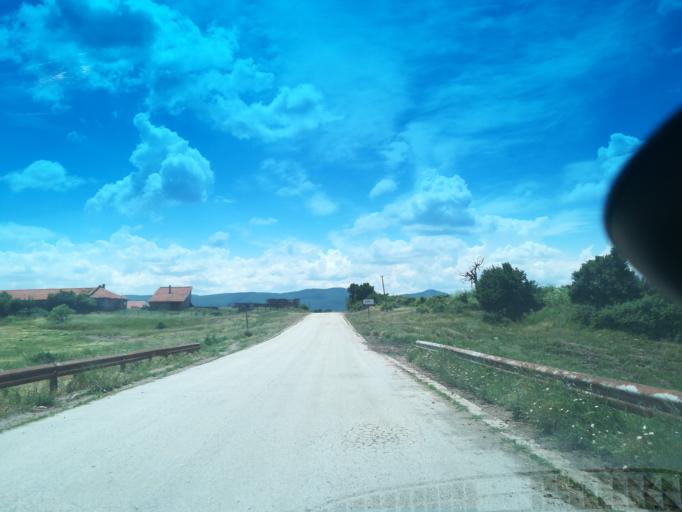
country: BG
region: Khaskovo
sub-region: Obshtina Mineralni Bani
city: Mineralni Bani
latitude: 41.9516
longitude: 25.2485
